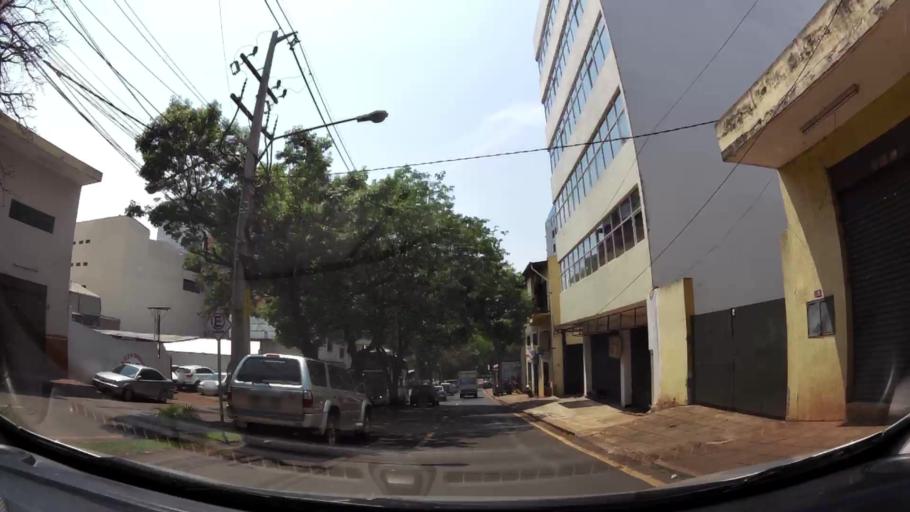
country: PY
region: Alto Parana
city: Ciudad del Este
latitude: -25.5139
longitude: -54.6114
